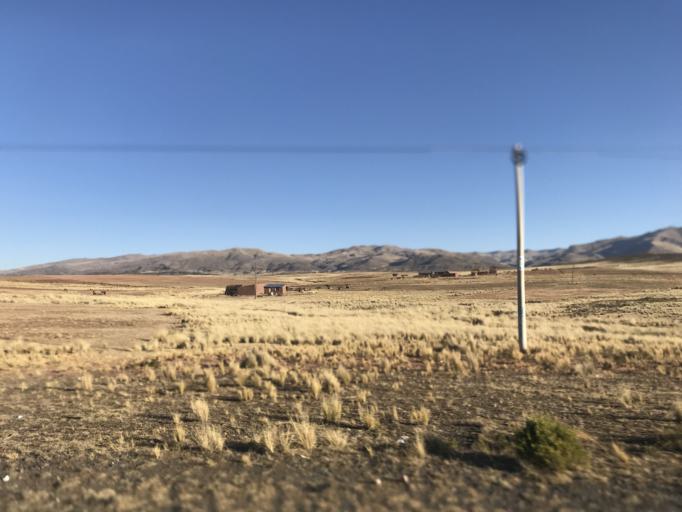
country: BO
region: La Paz
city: Tiahuanaco
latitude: -16.5631
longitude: -68.6273
